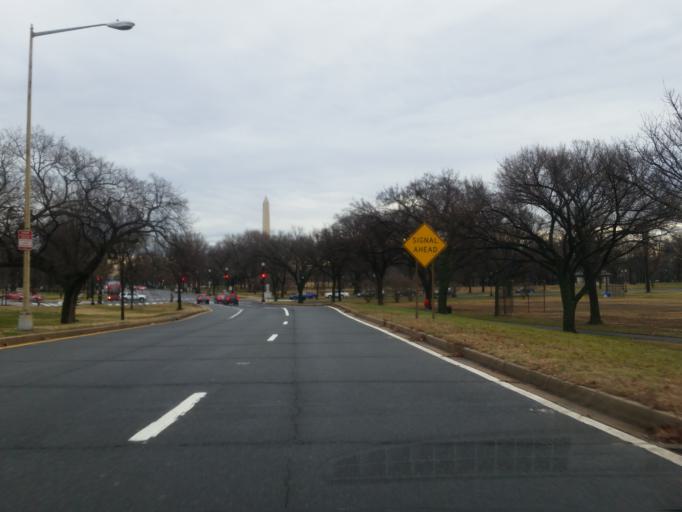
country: US
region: Washington, D.C.
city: Washington, D.C.
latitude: 38.8922
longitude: -77.0519
